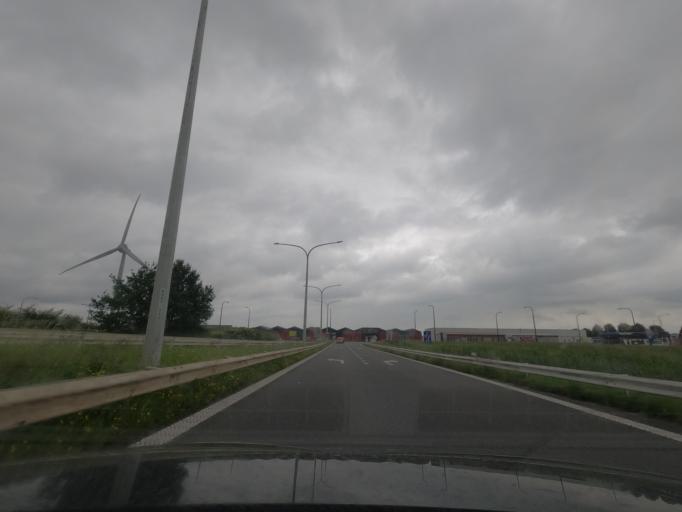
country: BE
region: Wallonia
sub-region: Province de Namur
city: Floreffe
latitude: 50.4943
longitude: 4.7220
